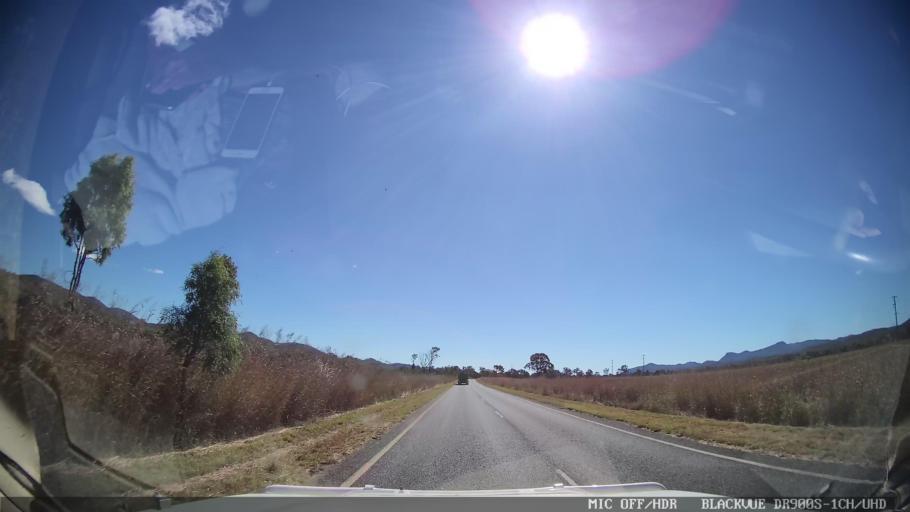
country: AU
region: Queensland
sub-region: Gladstone
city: Toolooa
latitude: -24.2816
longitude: 151.2792
